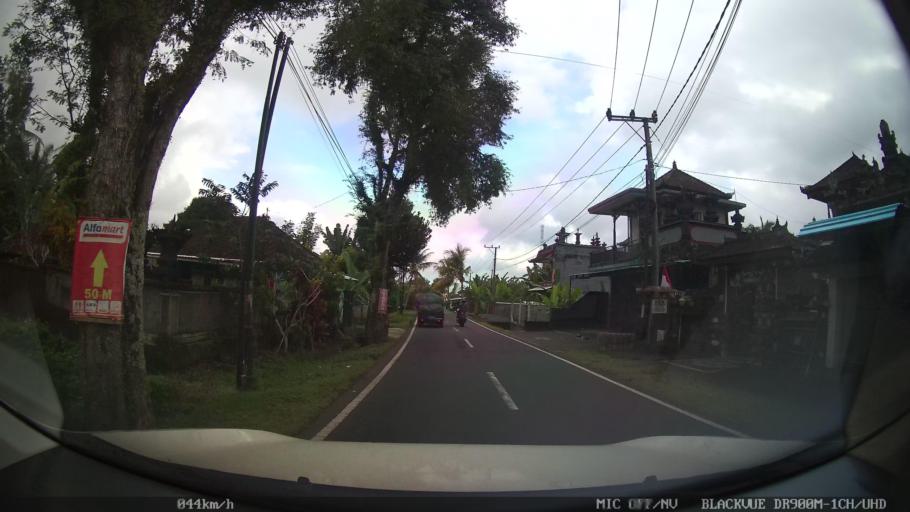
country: ID
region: Bali
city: Pohgending Kangin
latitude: -8.4331
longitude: 115.1431
